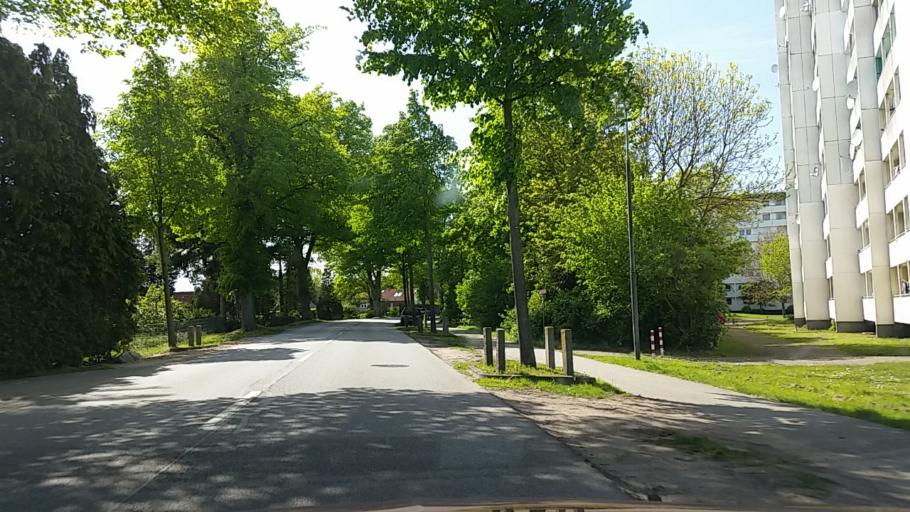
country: DE
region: Schleswig-Holstein
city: Stockelsdorf
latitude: 53.8498
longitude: 10.6367
